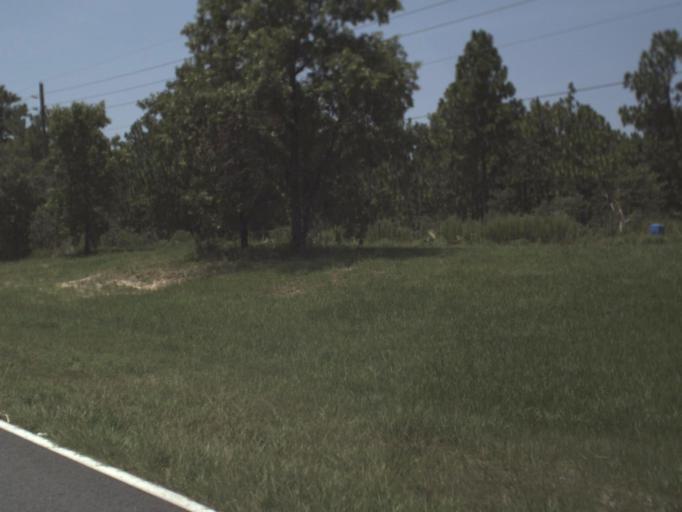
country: US
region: Florida
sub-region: Hernando County
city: North Weeki Wachee
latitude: 28.5839
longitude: -82.5549
